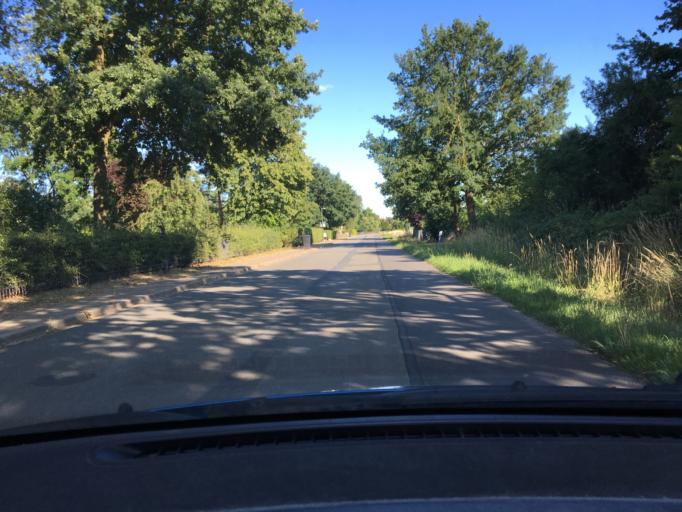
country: DE
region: Mecklenburg-Vorpommern
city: Boizenburg
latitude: 53.3526
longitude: 10.7085
